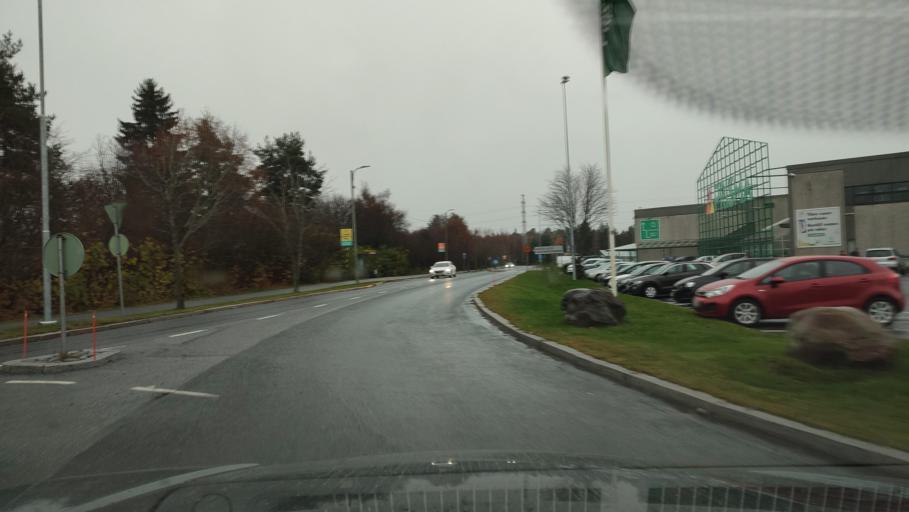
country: FI
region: Ostrobothnia
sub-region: Vaasa
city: Vaasa
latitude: 63.1036
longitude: 21.6481
